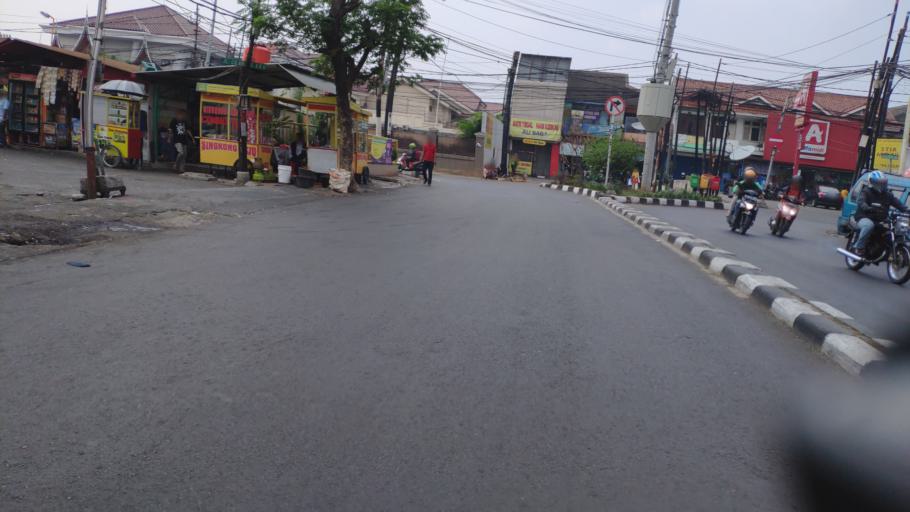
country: ID
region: West Java
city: Pamulang
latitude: -6.3104
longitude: 106.8137
